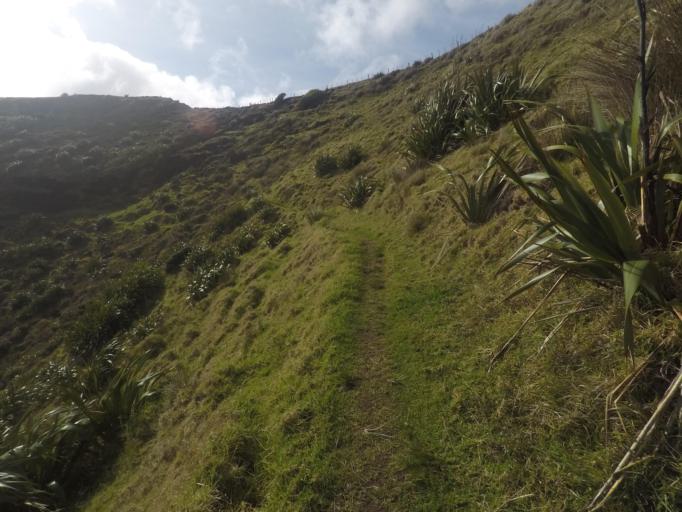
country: NZ
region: Auckland
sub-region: Auckland
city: Muriwai Beach
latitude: -36.8674
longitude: 174.4362
